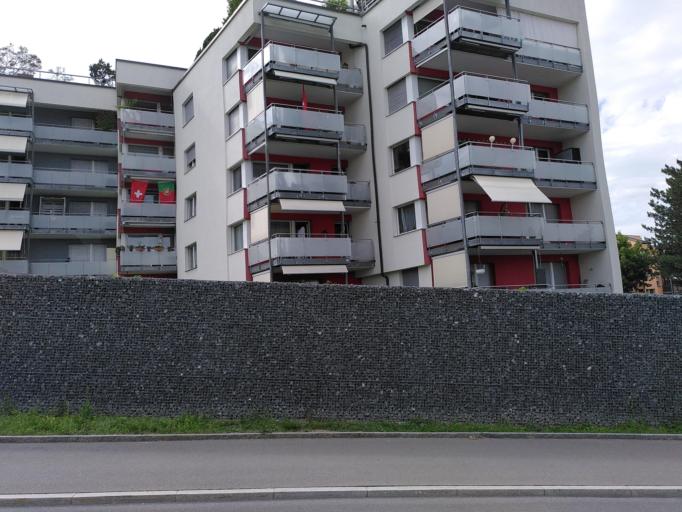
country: CH
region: Zurich
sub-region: Bezirk Horgen
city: Richterswil
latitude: 47.2053
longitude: 8.6954
